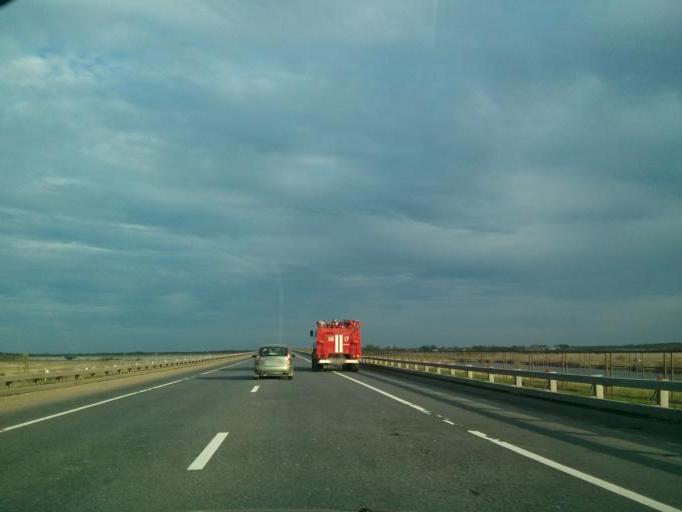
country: RU
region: Vladimir
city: Murom
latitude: 55.5925
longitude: 42.1156
